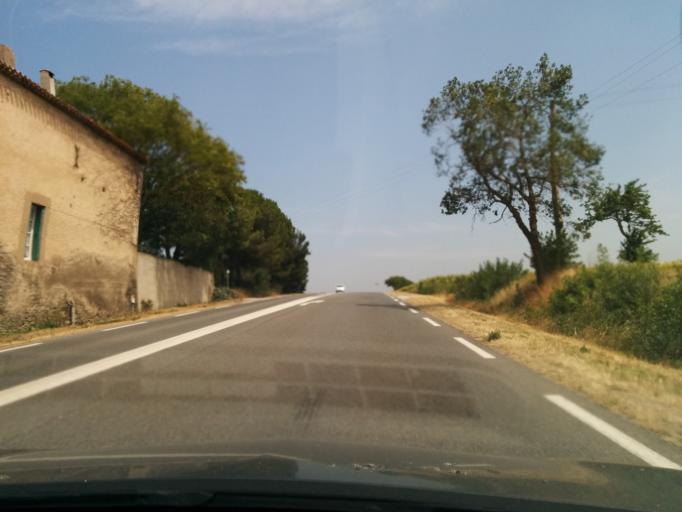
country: FR
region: Languedoc-Roussillon
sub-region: Departement de l'Aude
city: Pezens
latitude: 43.2600
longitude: 2.2347
